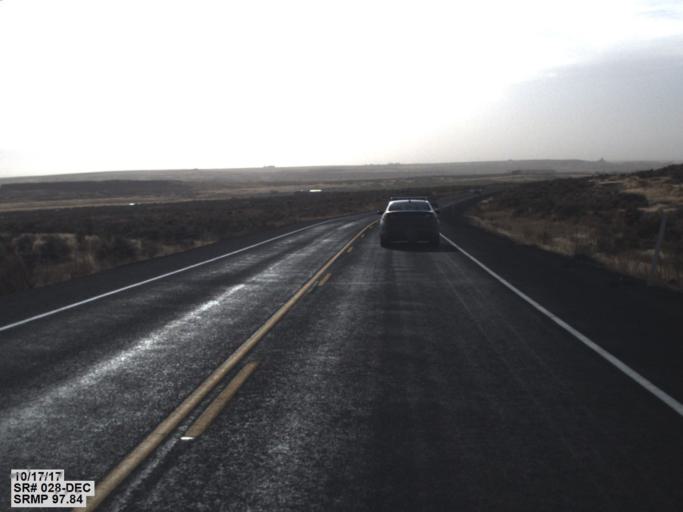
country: US
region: Washington
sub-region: Adams County
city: Ritzville
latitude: 47.3420
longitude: -118.6105
